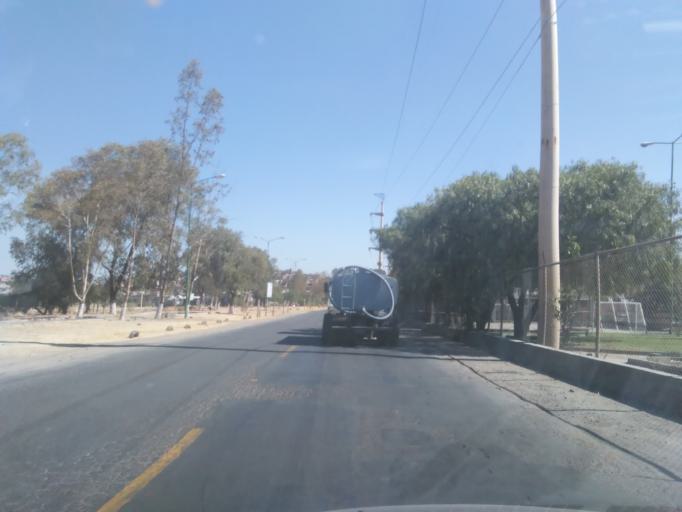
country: BO
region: Cochabamba
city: Cochabamba
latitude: -17.3996
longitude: -66.1385
